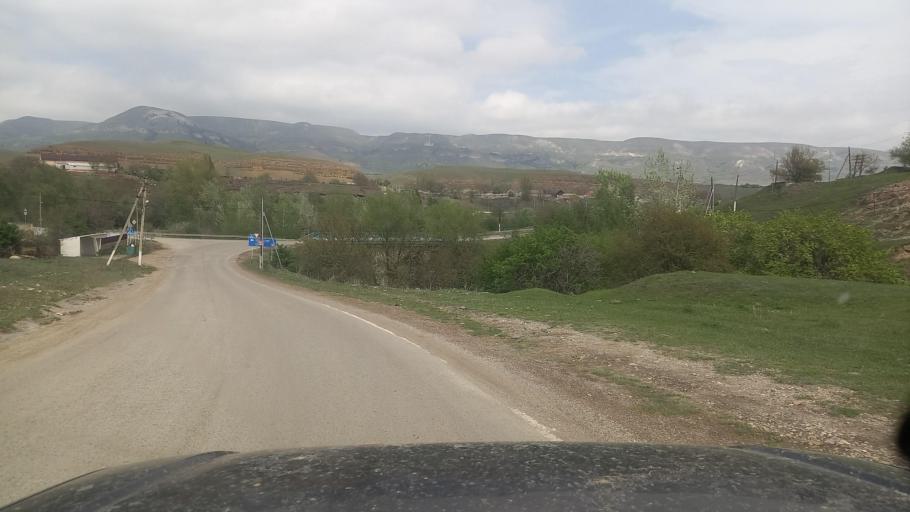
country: RU
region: Kabardino-Balkariya
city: Kamennomostskoye
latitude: 43.7332
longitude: 43.0477
